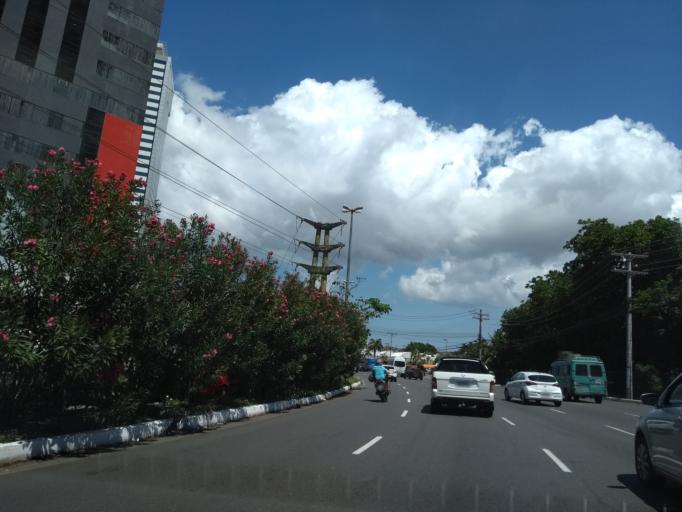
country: BR
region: Bahia
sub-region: Salvador
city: Salvador
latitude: -12.9800
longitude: -38.4503
